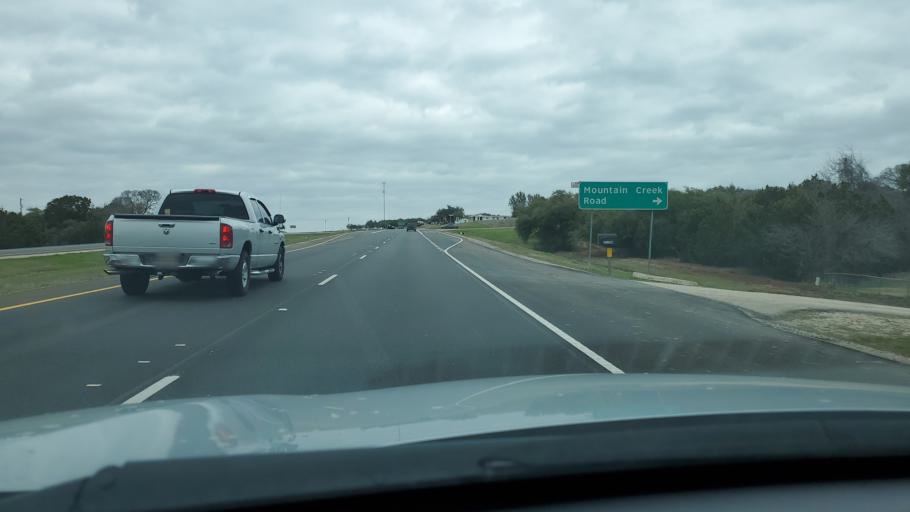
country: US
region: Texas
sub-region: Williamson County
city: Florence
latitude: 30.9252
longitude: -97.7935
